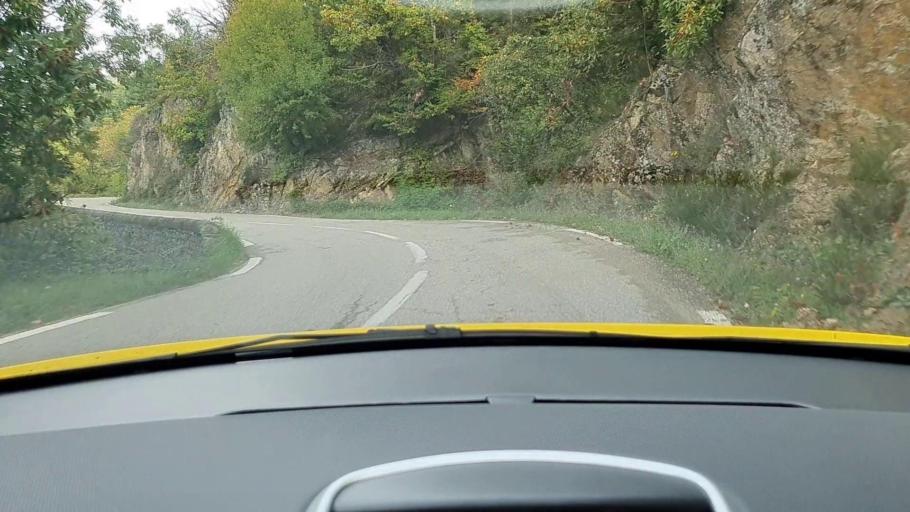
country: FR
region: Languedoc-Roussillon
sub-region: Departement du Gard
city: Le Vigan
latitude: 44.0155
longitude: 3.5981
